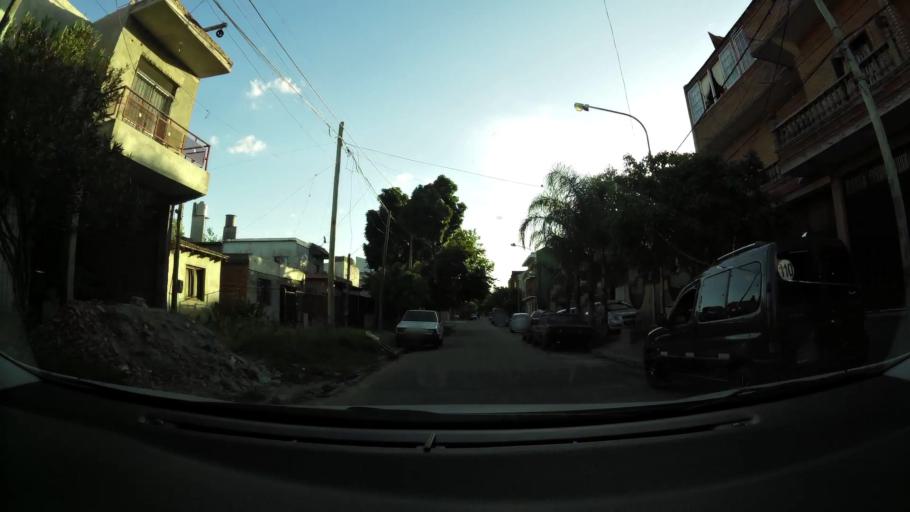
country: AR
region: Buenos Aires F.D.
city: Villa Lugano
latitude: -34.6968
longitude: -58.4810
